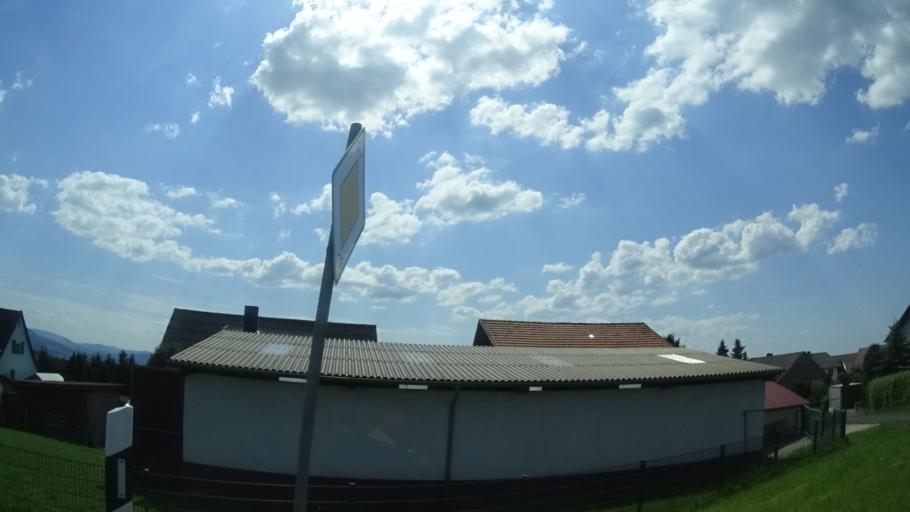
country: DE
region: Thuringia
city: Andenhausen
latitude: 50.6651
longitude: 10.0452
